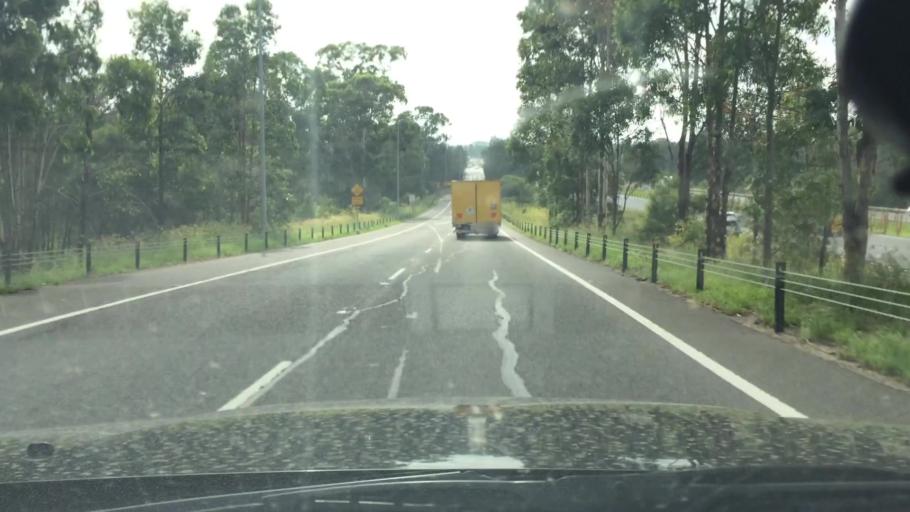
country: AU
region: New South Wales
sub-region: Blacktown
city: Doonside
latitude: -33.7986
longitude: 150.8586
